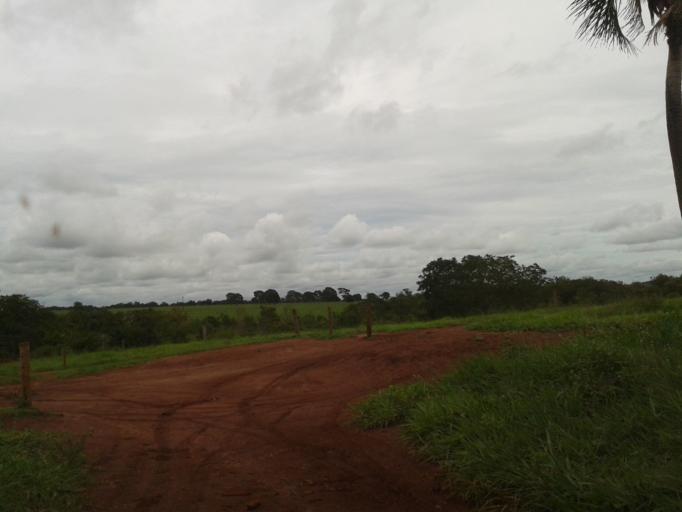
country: BR
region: Minas Gerais
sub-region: Capinopolis
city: Capinopolis
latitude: -18.7953
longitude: -49.7869
